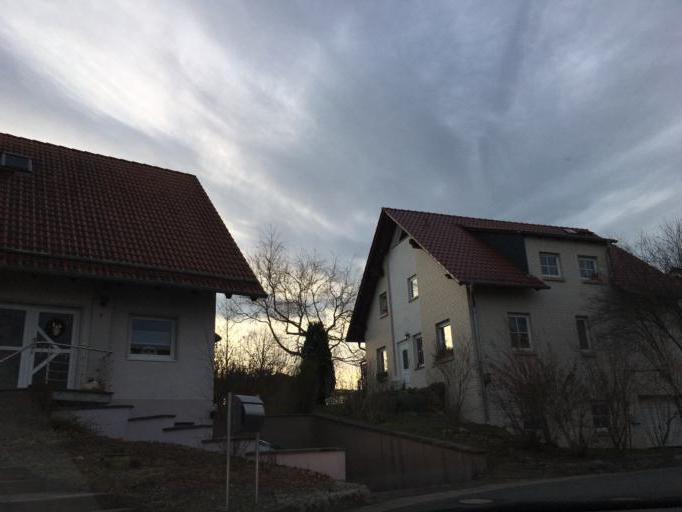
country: DE
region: Thuringia
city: Bad Berka
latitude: 50.9013
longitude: 11.2730
